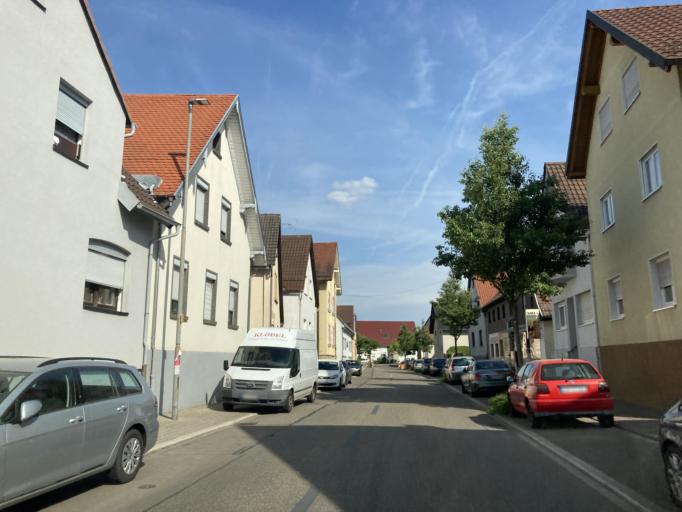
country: DE
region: Baden-Wuerttemberg
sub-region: Karlsruhe Region
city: Karlsdorf-Neuthard
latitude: 49.1121
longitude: 8.5112
